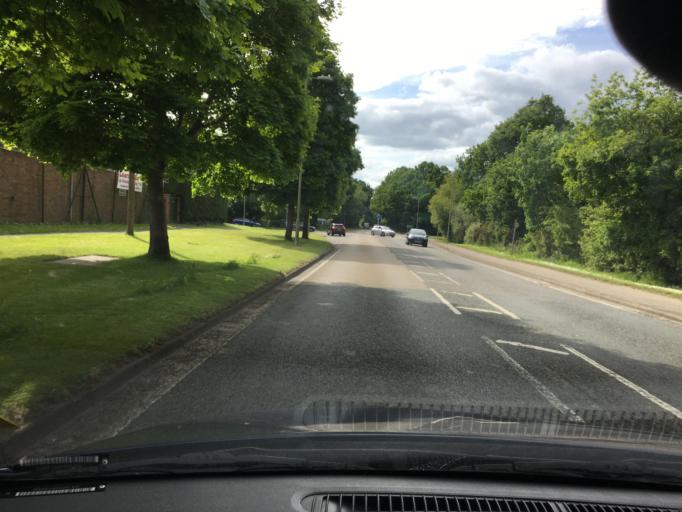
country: GB
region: England
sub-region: Hampshire
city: Yateley
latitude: 51.3432
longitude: -0.8370
